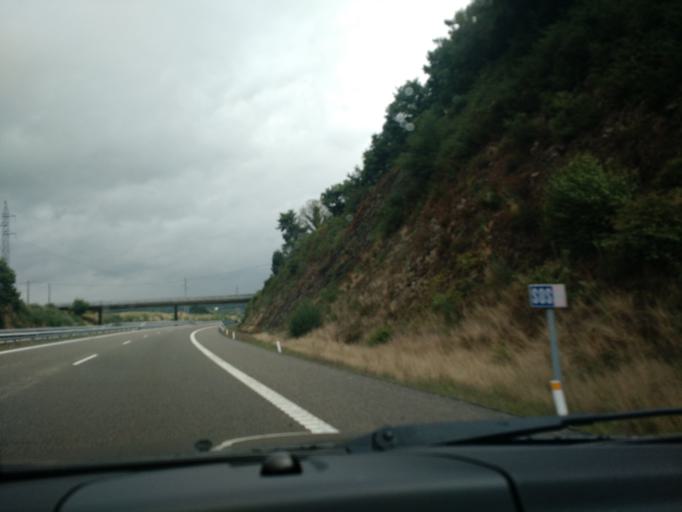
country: ES
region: Galicia
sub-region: Provincia da Coruna
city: Oroso
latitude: 42.9602
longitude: -8.4566
